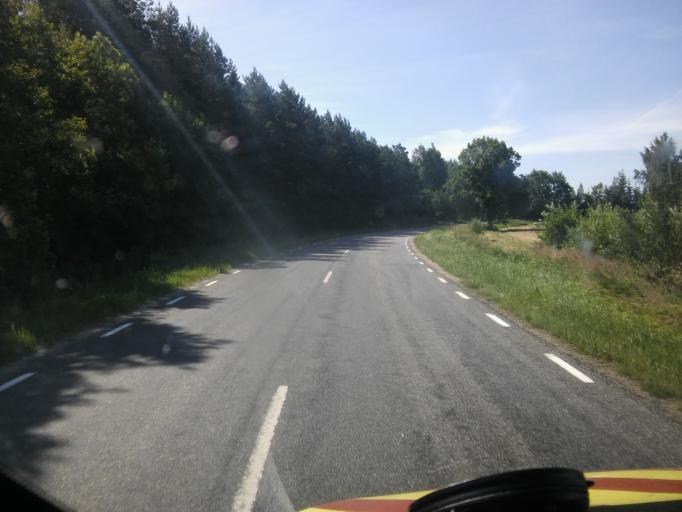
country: EE
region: Paernumaa
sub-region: Paikuse vald
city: Paikuse
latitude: 58.3084
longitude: 24.6902
